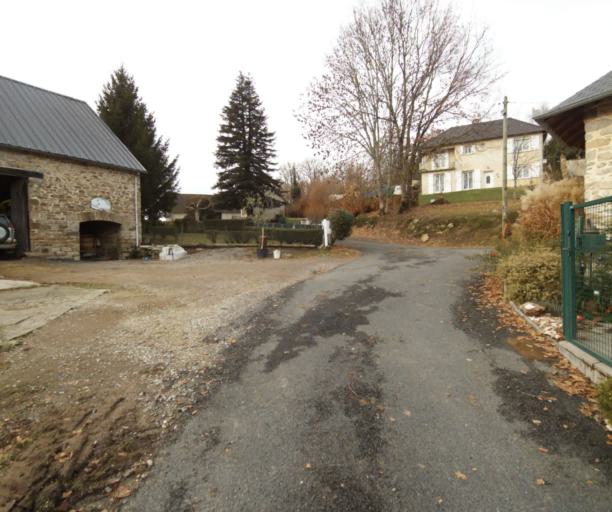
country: FR
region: Limousin
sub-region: Departement de la Correze
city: Saint-Mexant
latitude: 45.2618
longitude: 1.6498
